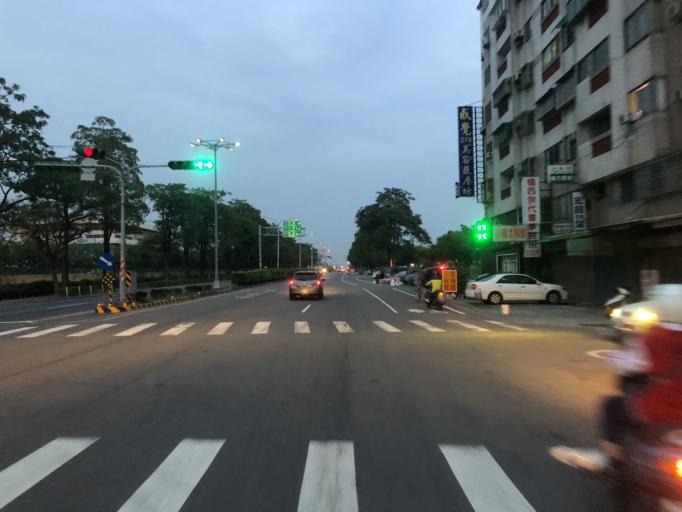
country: TW
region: Taiwan
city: Yujing
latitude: 23.1284
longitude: 120.3193
